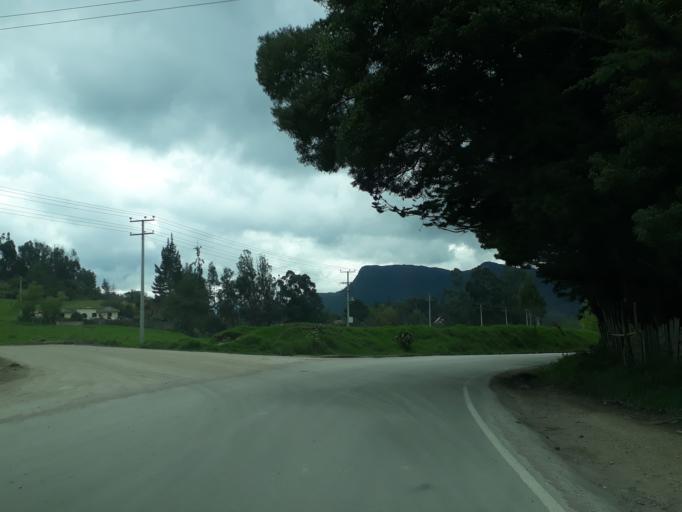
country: CO
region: Cundinamarca
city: Ubate
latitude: 5.3242
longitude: -73.7643
